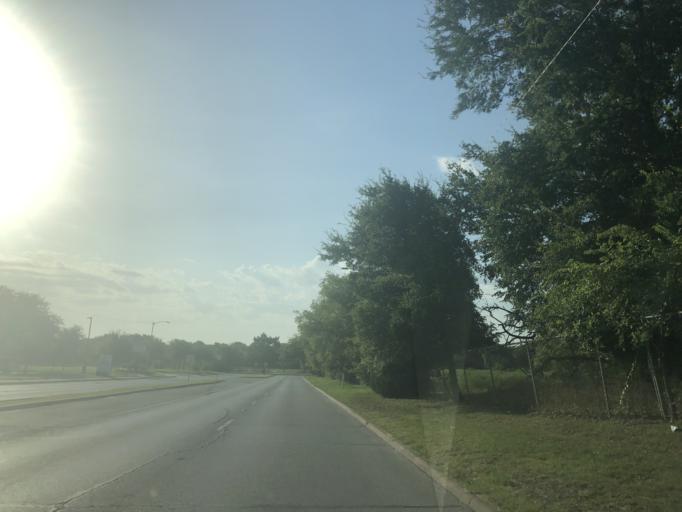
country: US
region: Texas
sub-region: Dallas County
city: Grand Prairie
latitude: 32.7688
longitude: -97.0234
